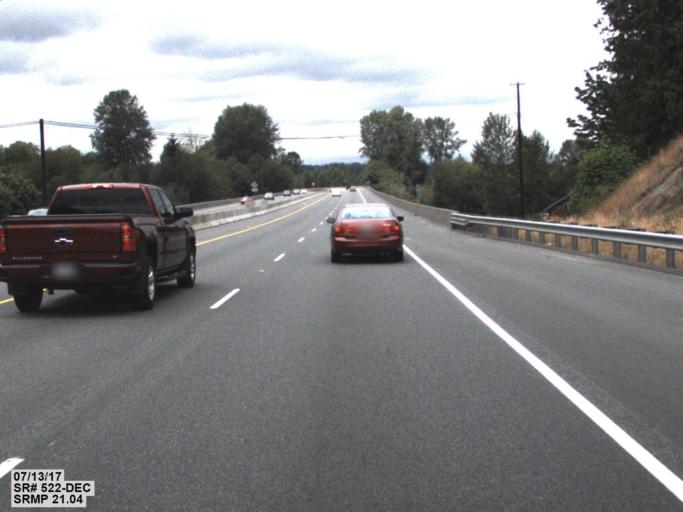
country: US
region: Washington
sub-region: Snohomish County
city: Cathcart
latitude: 47.8305
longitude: -122.0388
